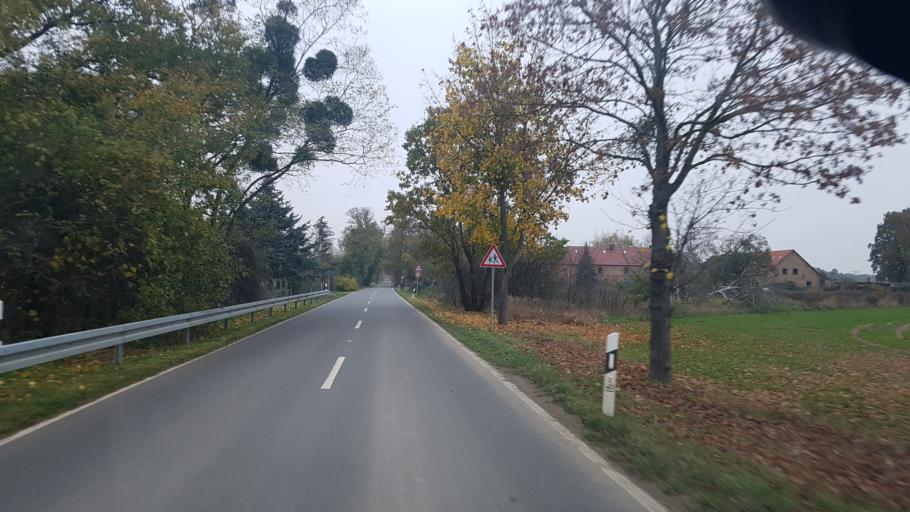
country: DE
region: Brandenburg
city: Lindow
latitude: 52.9499
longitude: 13.0094
